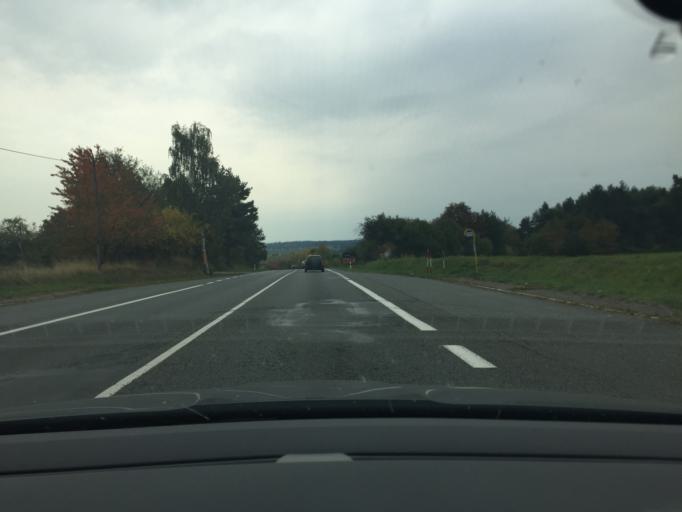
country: CZ
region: Central Bohemia
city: Milin
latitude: 49.6214
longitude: 14.0528
